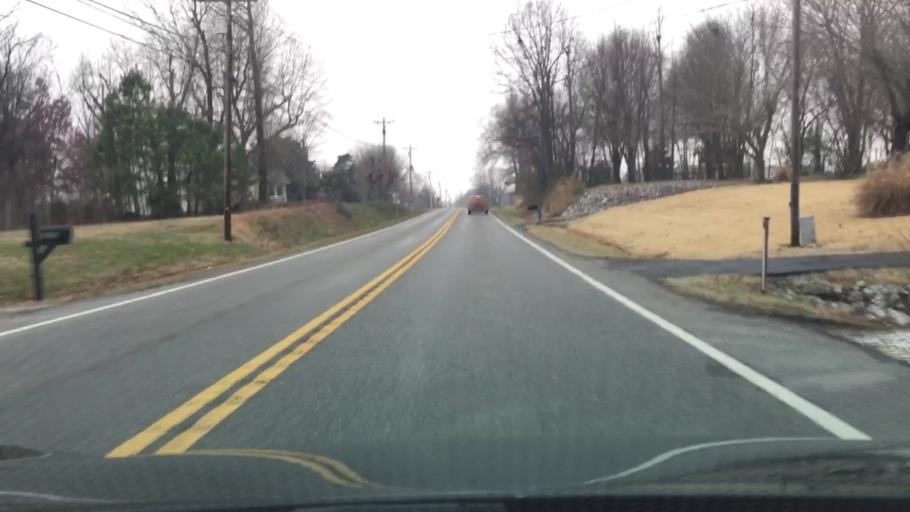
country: US
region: Kentucky
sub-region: Livingston County
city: Ledbetter
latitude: 36.9722
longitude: -88.4657
